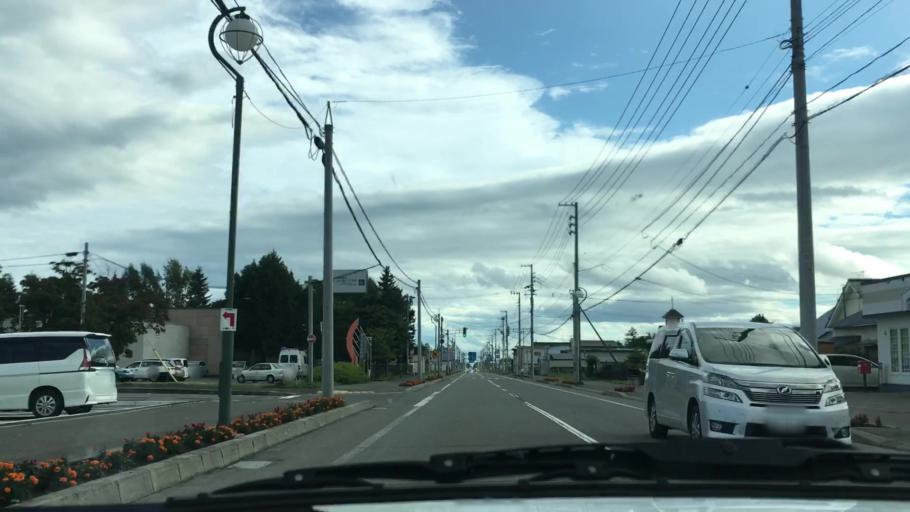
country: JP
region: Hokkaido
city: Otofuke
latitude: 43.2318
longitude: 143.2949
